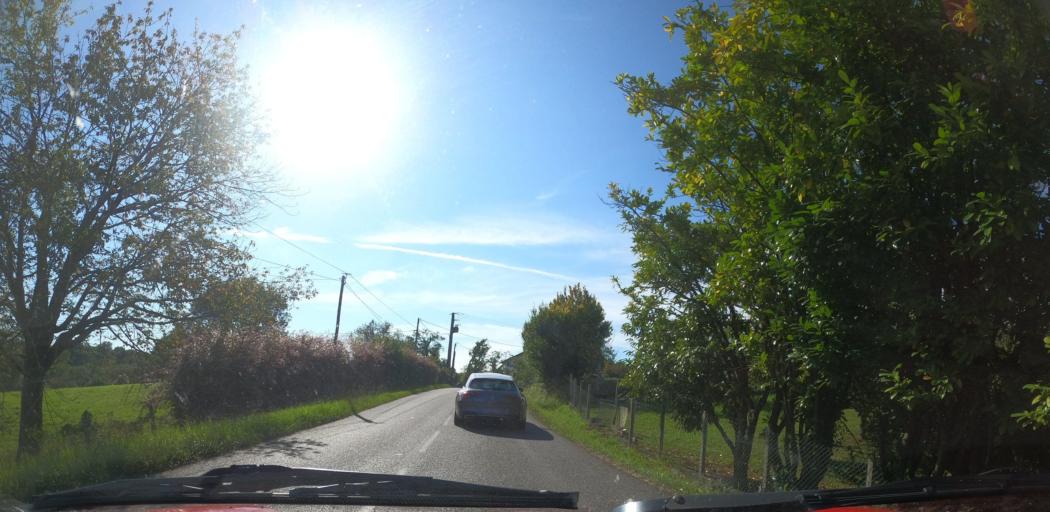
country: FR
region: Aquitaine
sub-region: Departement des Pyrenees-Atlantiques
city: Saint-Pee-sur-Nivelle
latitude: 43.3665
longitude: -1.5452
